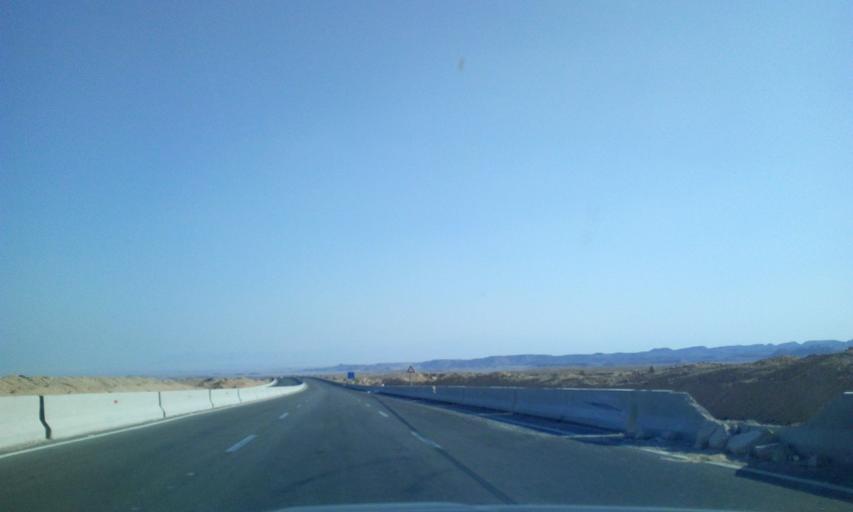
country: EG
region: As Suways
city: Ain Sukhna
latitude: 29.2777
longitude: 32.4689
